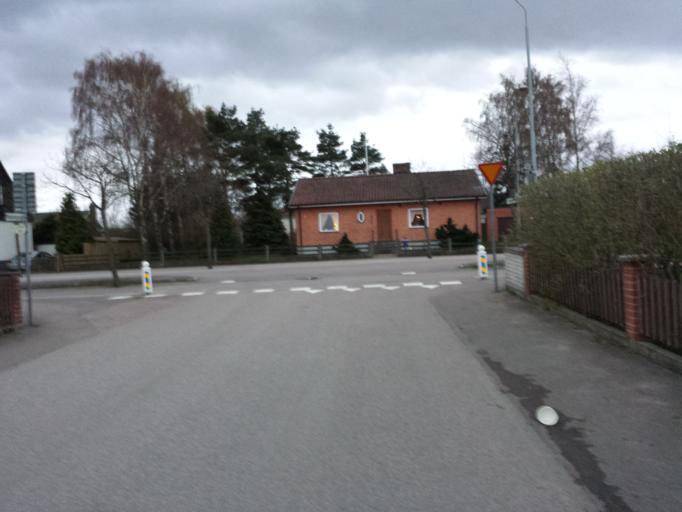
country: SE
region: Skane
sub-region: Sjobo Kommun
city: Sjoebo
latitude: 55.6336
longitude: 13.6993
